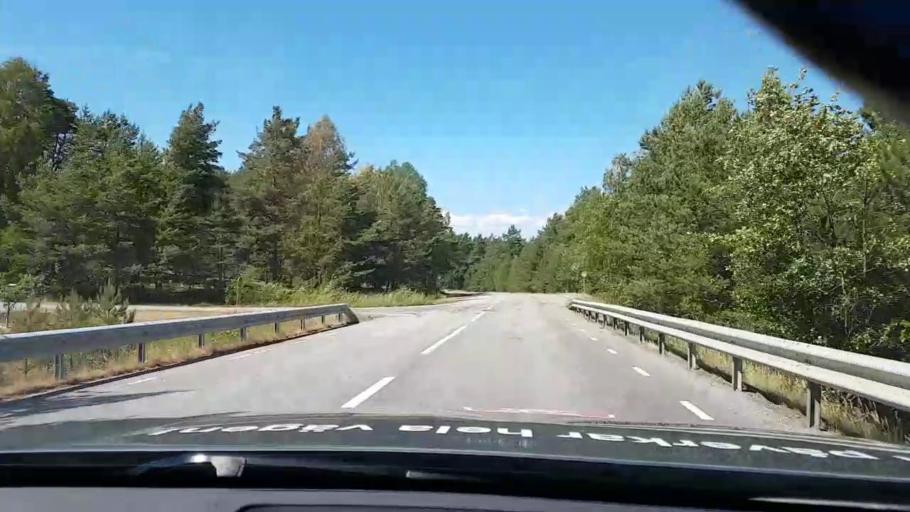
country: SE
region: Kalmar
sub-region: Vasterviks Kommun
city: Forserum
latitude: 57.9204
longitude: 16.5875
